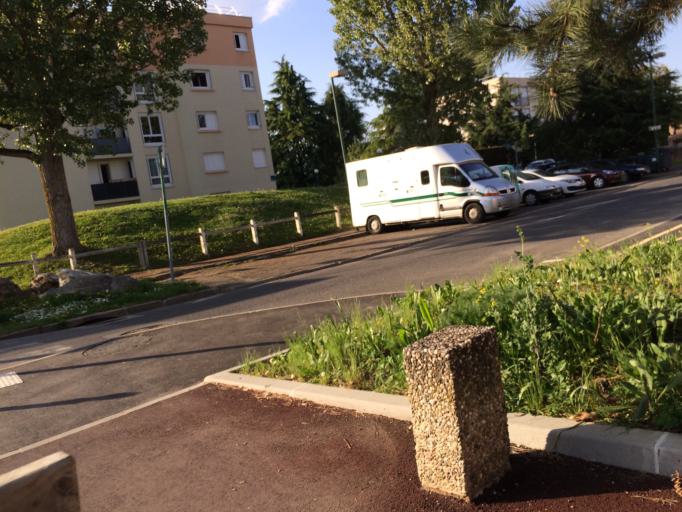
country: FR
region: Ile-de-France
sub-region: Departement de l'Essonne
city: Verrieres-le-Buisson
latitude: 48.7523
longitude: 2.2700
